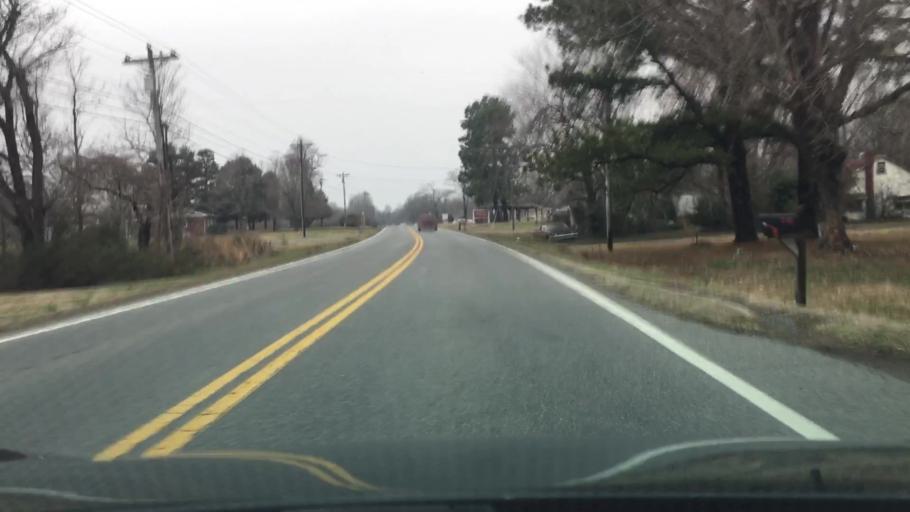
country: US
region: Kentucky
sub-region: Marshall County
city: Calvert City
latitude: 36.9718
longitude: -88.3930
